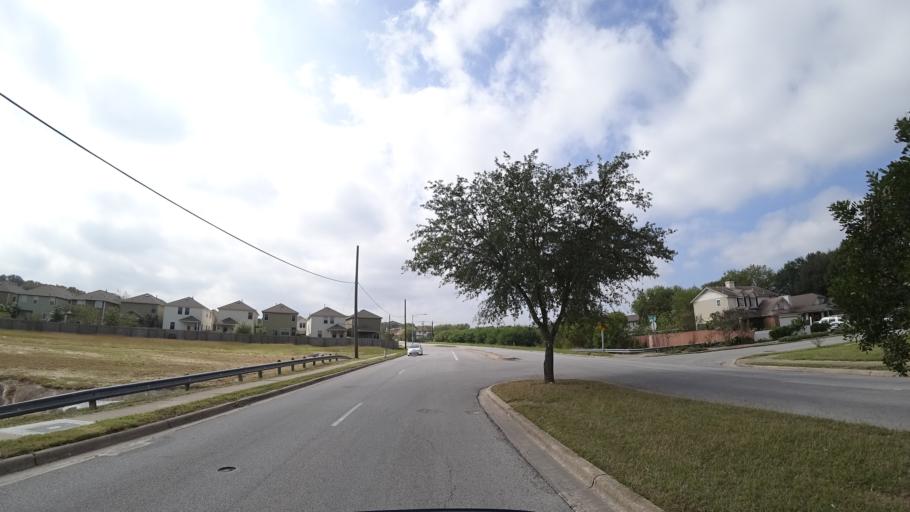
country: US
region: Texas
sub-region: Travis County
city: Shady Hollow
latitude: 30.1959
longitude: -97.8295
